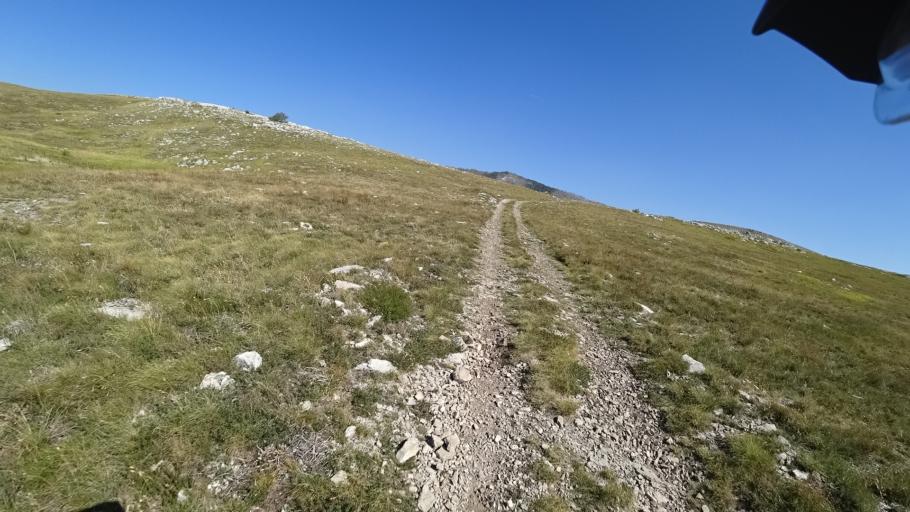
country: HR
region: Splitsko-Dalmatinska
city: Hrvace
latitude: 43.9039
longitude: 16.6073
